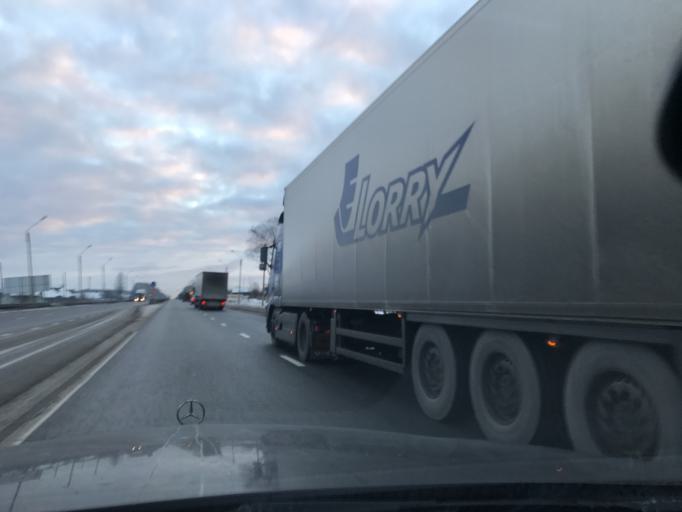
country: RU
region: Vladimir
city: Krasnyy Oktyabr'
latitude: 56.2191
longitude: 41.4761
